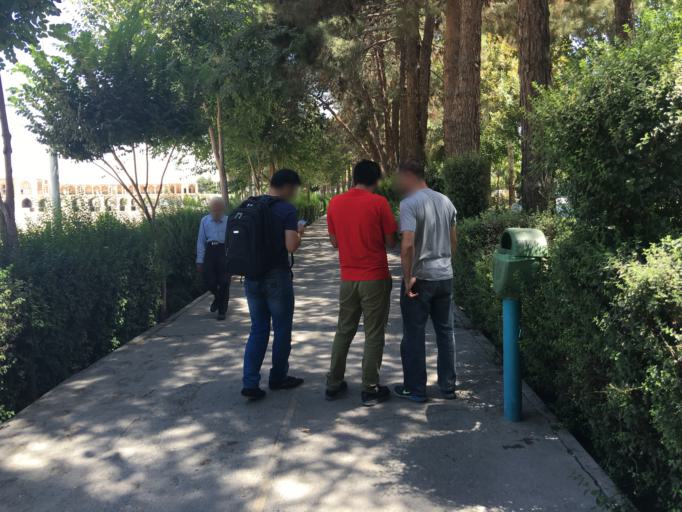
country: IR
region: Isfahan
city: Isfahan
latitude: 32.6358
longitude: 51.6809
